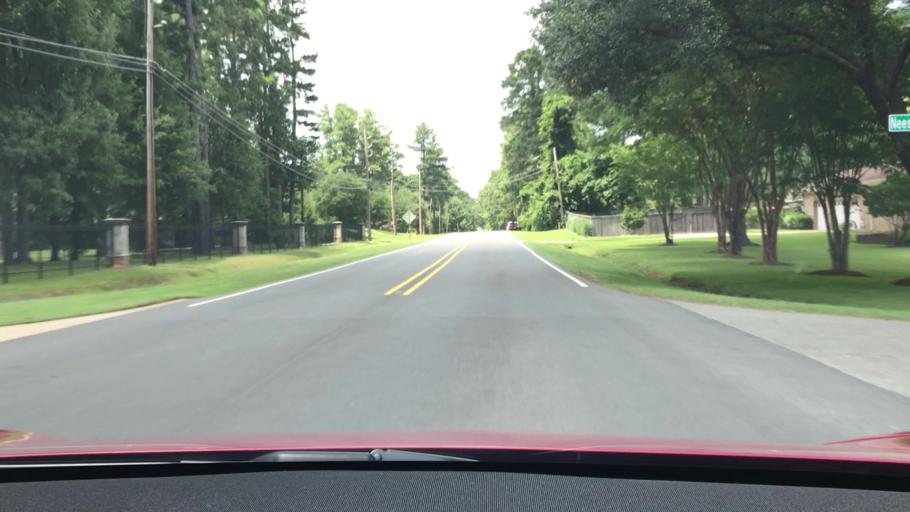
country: US
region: Louisiana
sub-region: De Soto Parish
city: Stonewall
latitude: 32.3720
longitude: -93.7137
